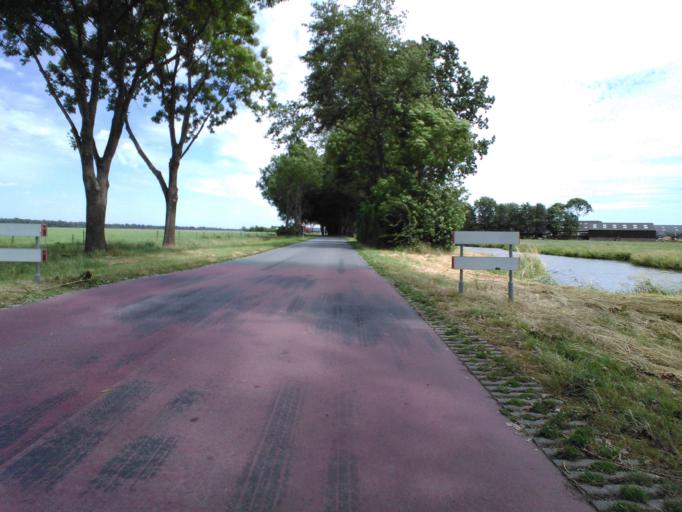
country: NL
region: South Holland
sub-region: Gemeente Sliedrecht
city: Sliedrecht
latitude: 51.8398
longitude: 4.8095
